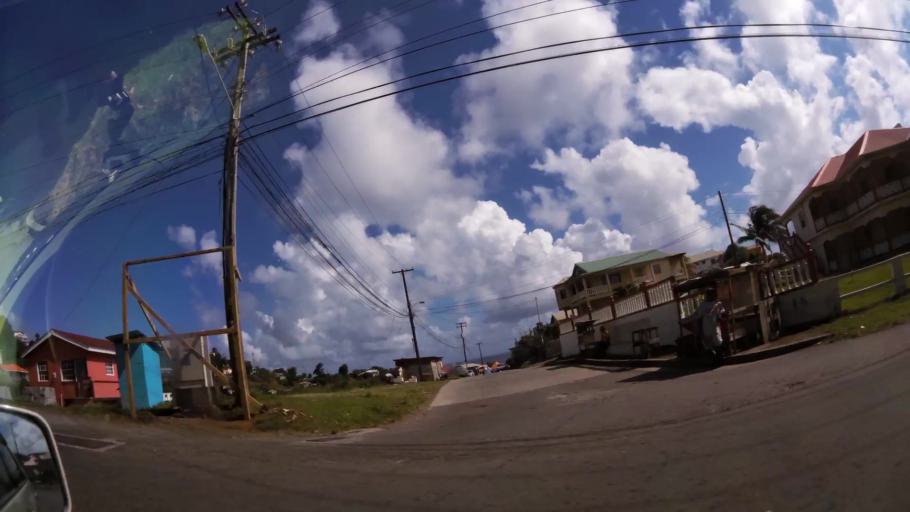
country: VC
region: Saint George
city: Kingstown
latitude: 13.1439
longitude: -61.1673
